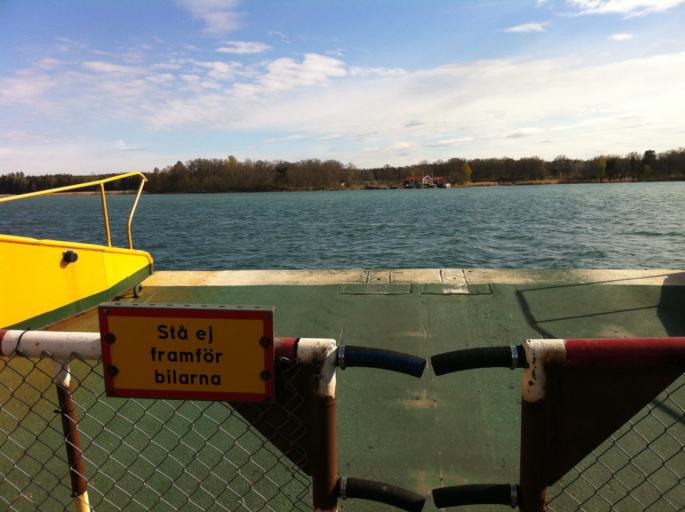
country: SE
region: Soedermanland
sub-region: Nykopings Kommun
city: Olstorp
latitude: 58.6354
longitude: 16.5946
